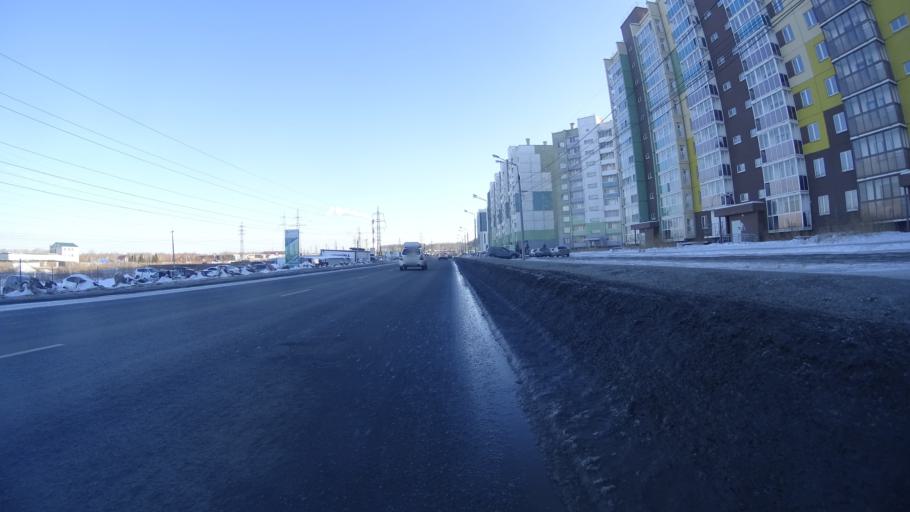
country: RU
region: Chelyabinsk
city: Roshchino
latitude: 55.2165
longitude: 61.3021
